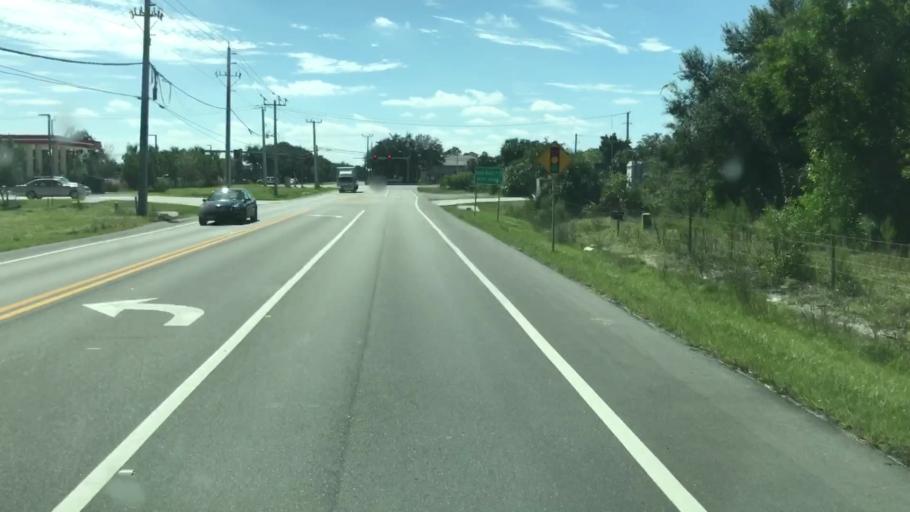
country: US
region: Florida
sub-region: Lee County
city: Bonita Springs
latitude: 26.3331
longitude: -81.7386
